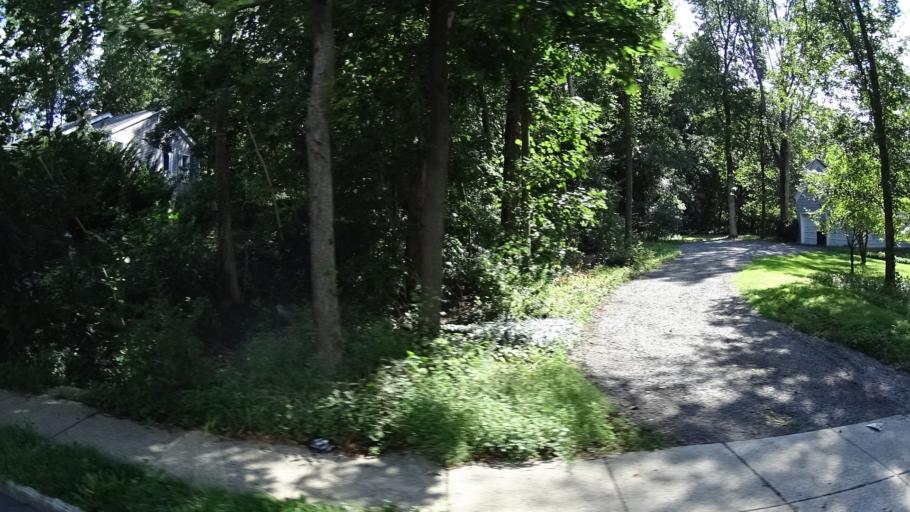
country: US
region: New Jersey
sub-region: Morris County
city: Chatham
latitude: 40.7187
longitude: -74.3840
